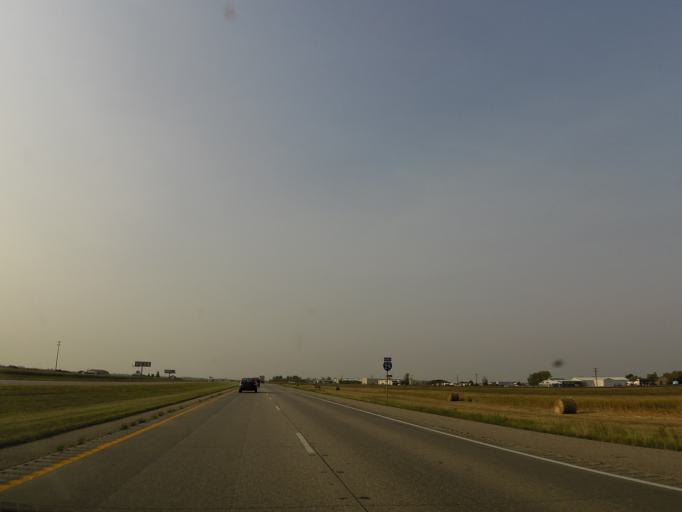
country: US
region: Minnesota
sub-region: Clay County
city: Oakport
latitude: 46.9405
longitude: -96.8538
